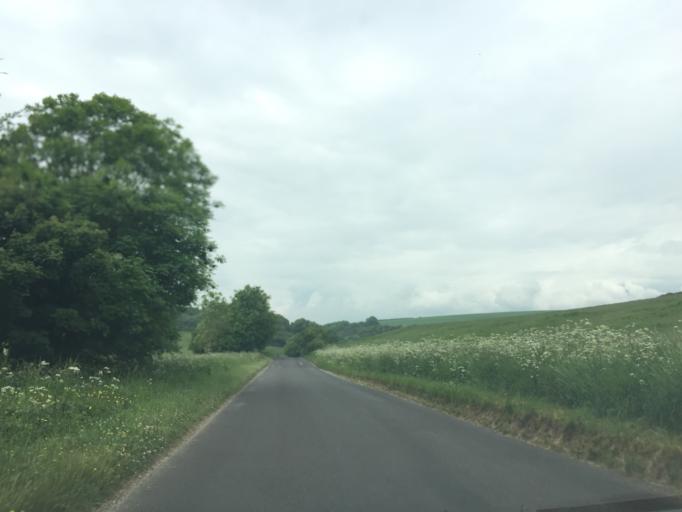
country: GB
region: England
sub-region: Dorset
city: Wool
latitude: 50.6407
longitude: -2.2670
